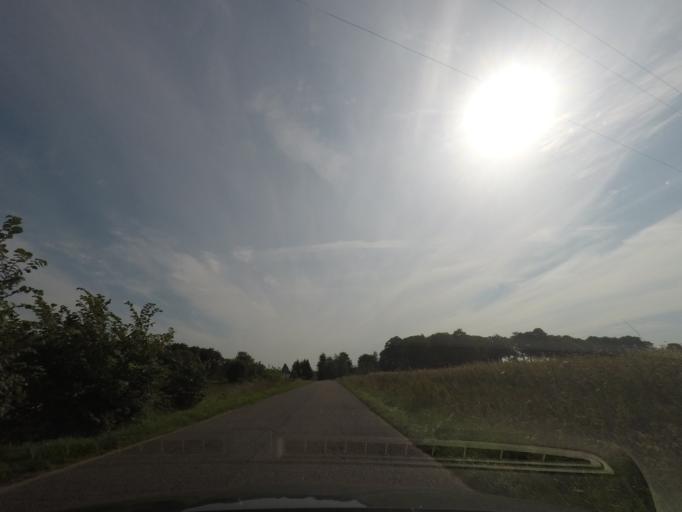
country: PL
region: Pomeranian Voivodeship
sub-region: Powiat slupski
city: Smoldzino
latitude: 54.6281
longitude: 17.2440
